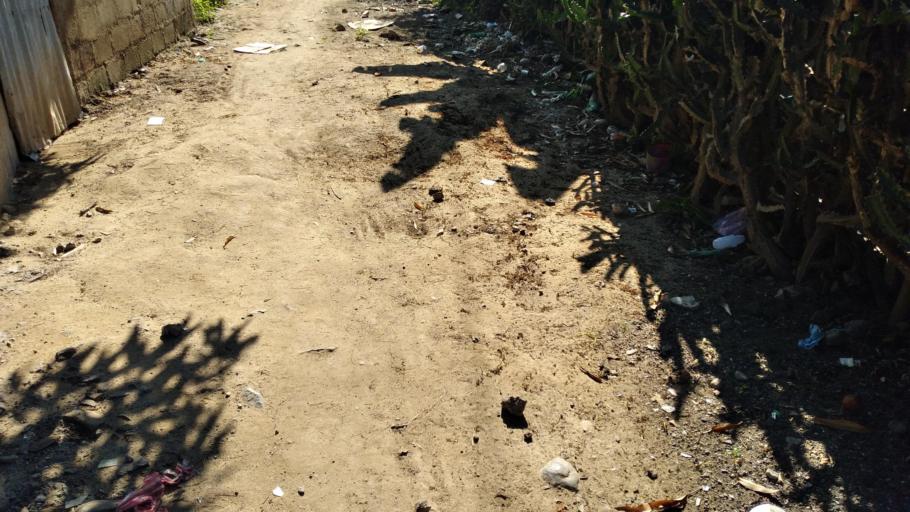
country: HT
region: Nord
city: Limonade
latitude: 19.6704
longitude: -72.1294
